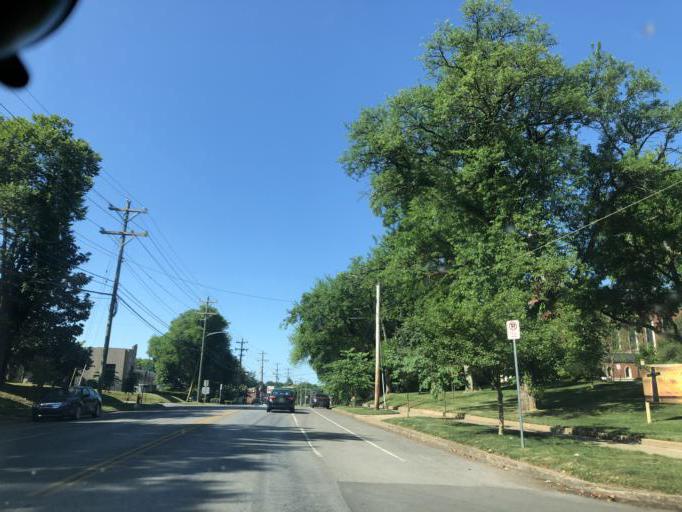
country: US
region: Tennessee
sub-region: Davidson County
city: Oak Hill
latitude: 36.1193
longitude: -86.7959
